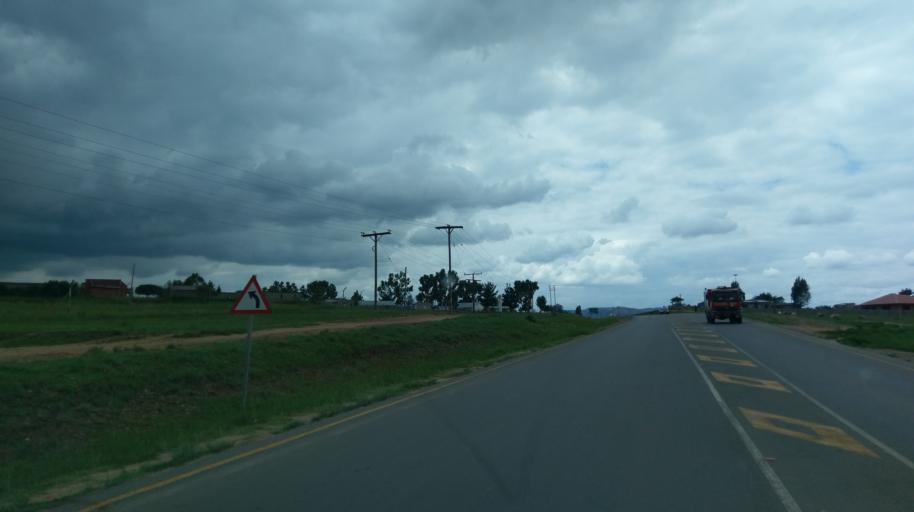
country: LS
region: Leribe
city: Maputsoe
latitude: -28.9132
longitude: 27.9181
